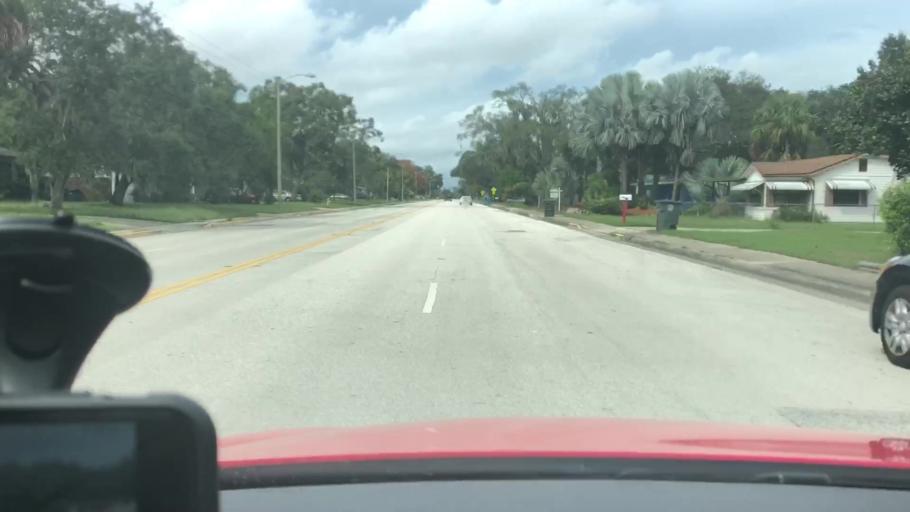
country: US
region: Florida
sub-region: Volusia County
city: Daytona Beach
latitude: 29.2106
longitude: -81.0507
